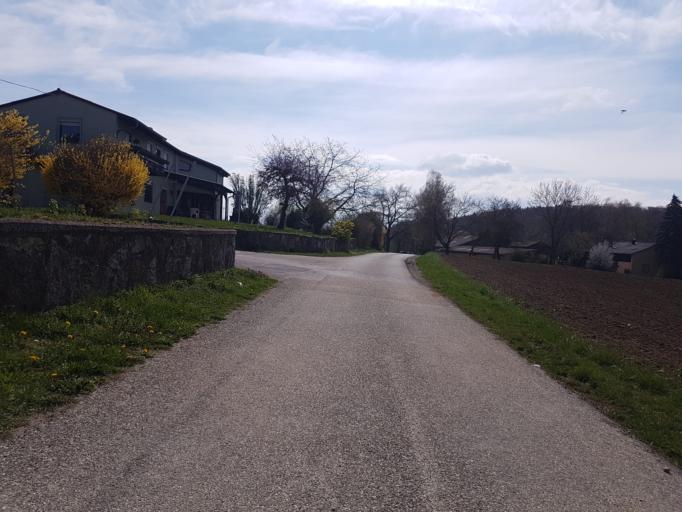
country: DE
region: Baden-Wuerttemberg
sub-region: Regierungsbezirk Stuttgart
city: Jagsthausen
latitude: 49.3813
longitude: 9.5157
